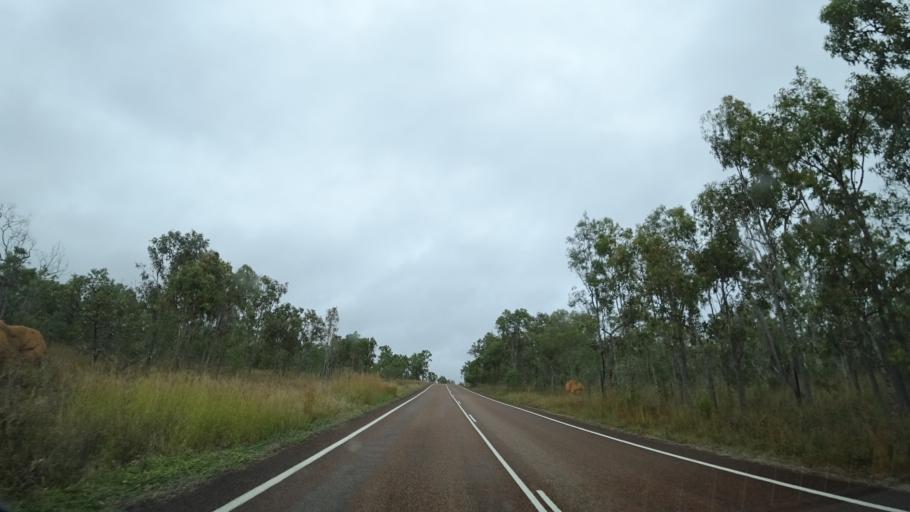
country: AU
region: Queensland
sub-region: Tablelands
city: Ravenshoe
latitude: -17.6820
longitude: 145.2334
